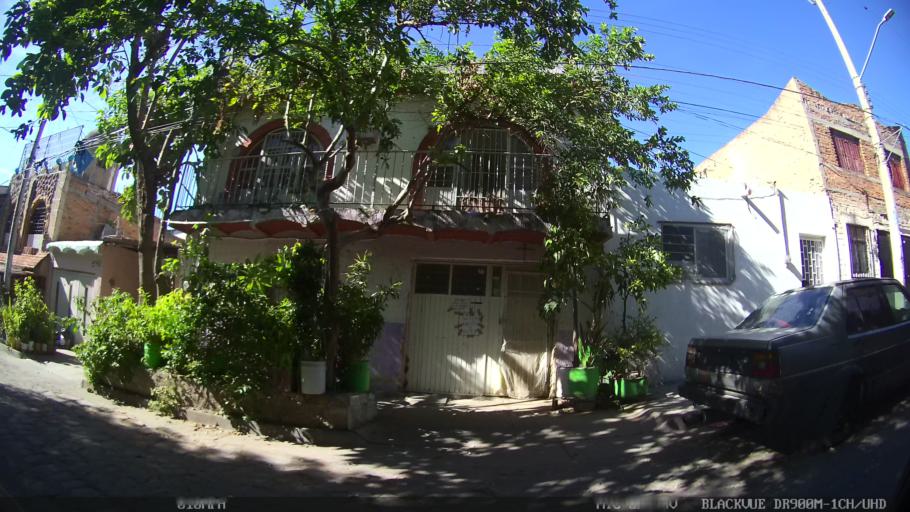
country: MX
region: Jalisco
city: Tlaquepaque
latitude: 20.6893
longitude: -103.2732
